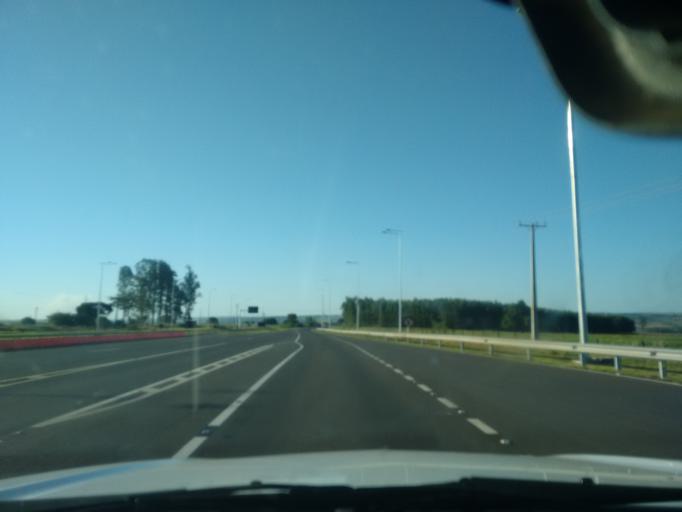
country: BR
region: Mato Grosso do Sul
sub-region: Eldorado
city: Eldorado
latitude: -23.8647
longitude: -54.3300
